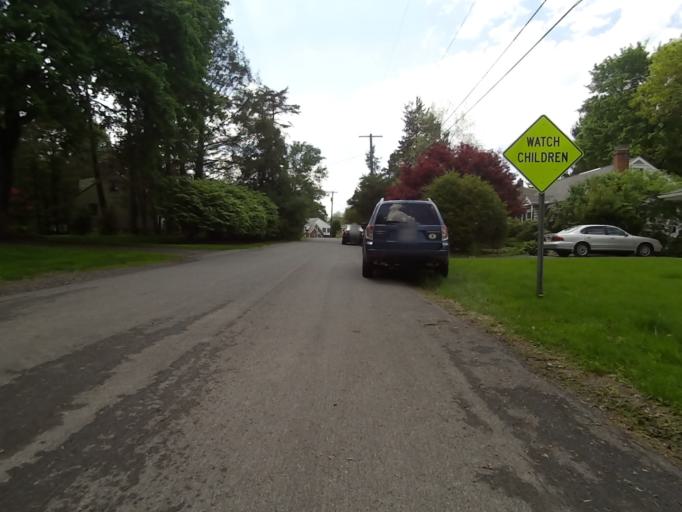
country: US
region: Pennsylvania
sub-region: Centre County
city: Houserville
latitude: 40.8129
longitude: -77.8389
